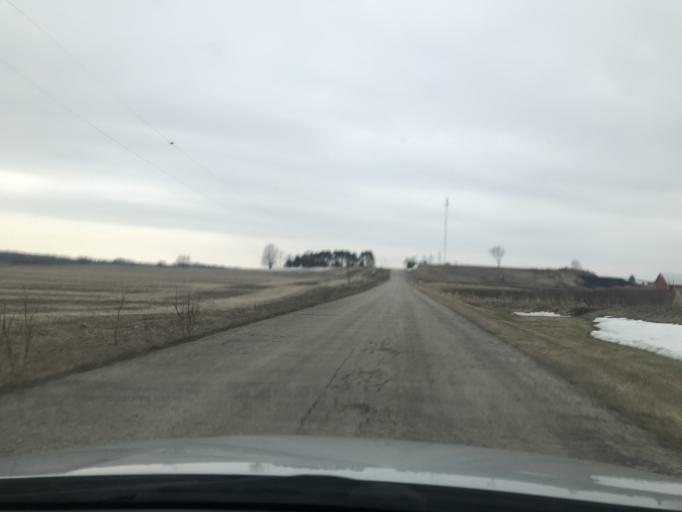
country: US
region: Wisconsin
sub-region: Marinette County
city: Peshtigo
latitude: 45.1005
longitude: -87.9323
